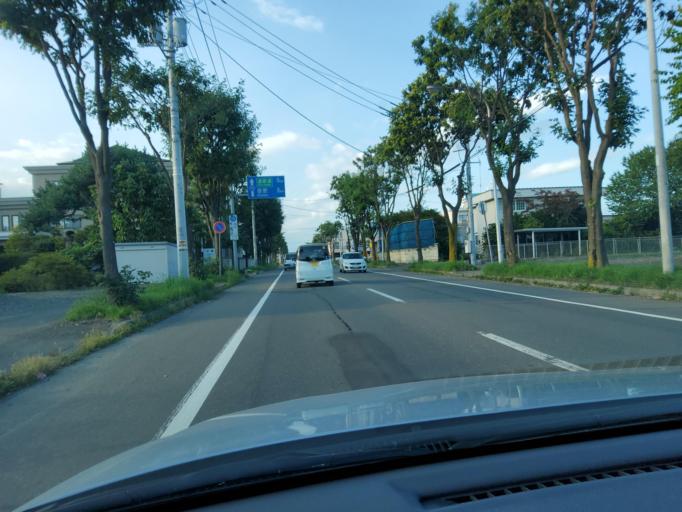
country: JP
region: Hokkaido
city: Obihiro
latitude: 42.9319
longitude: 143.1849
